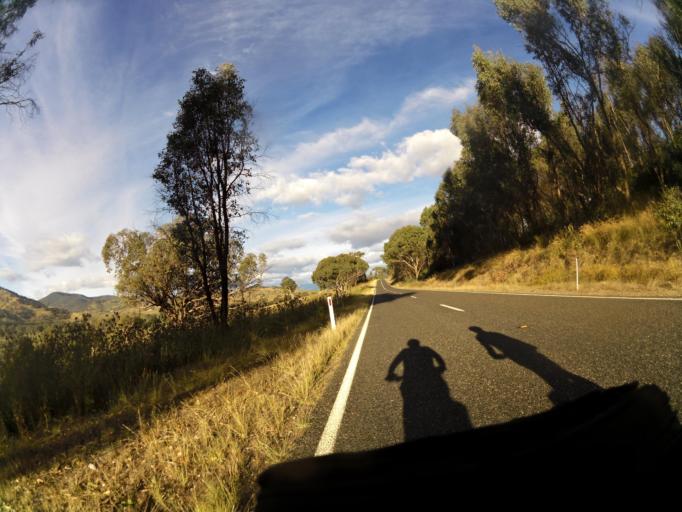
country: AU
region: New South Wales
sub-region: Greater Hume Shire
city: Holbrook
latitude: -36.0070
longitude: 147.9002
